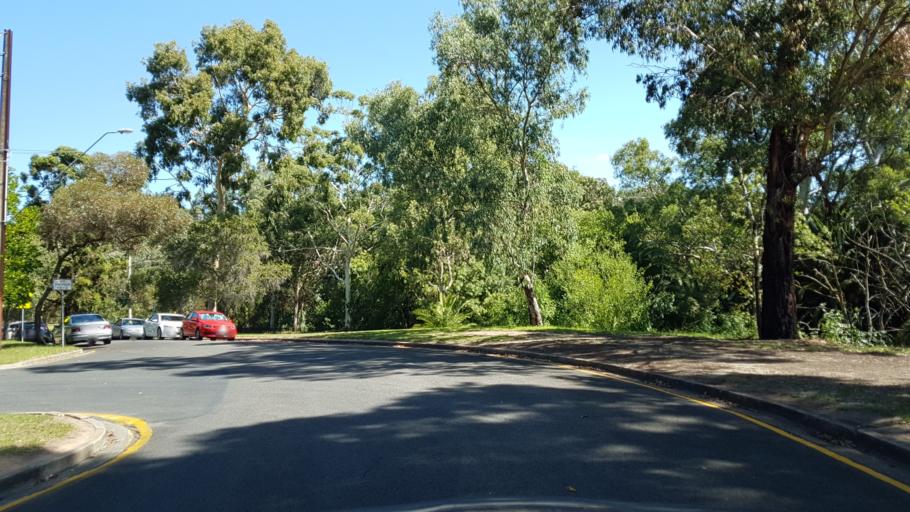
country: AU
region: South Australia
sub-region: Onkaparinga
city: Bedford Park
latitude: -35.0260
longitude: 138.5641
